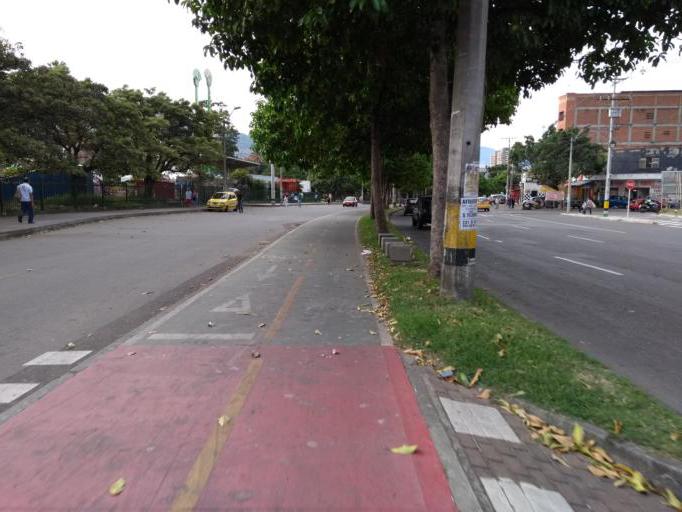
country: CO
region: Antioquia
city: Medellin
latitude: 6.2507
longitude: -75.5831
